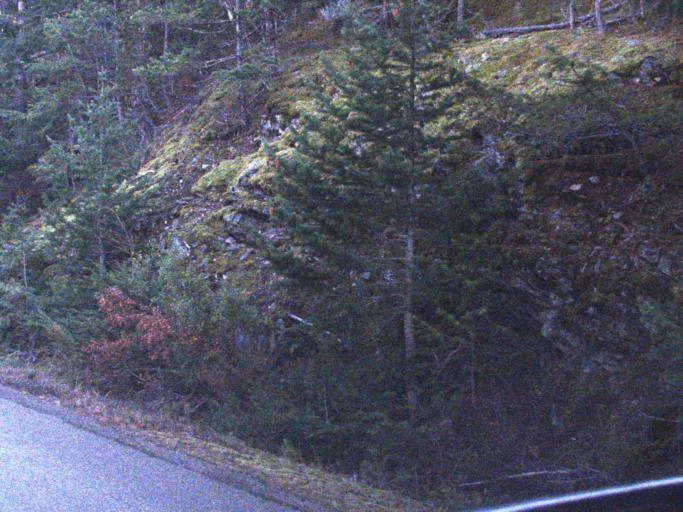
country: US
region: Washington
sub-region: Snohomish County
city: Darrington
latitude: 48.7281
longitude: -121.0464
